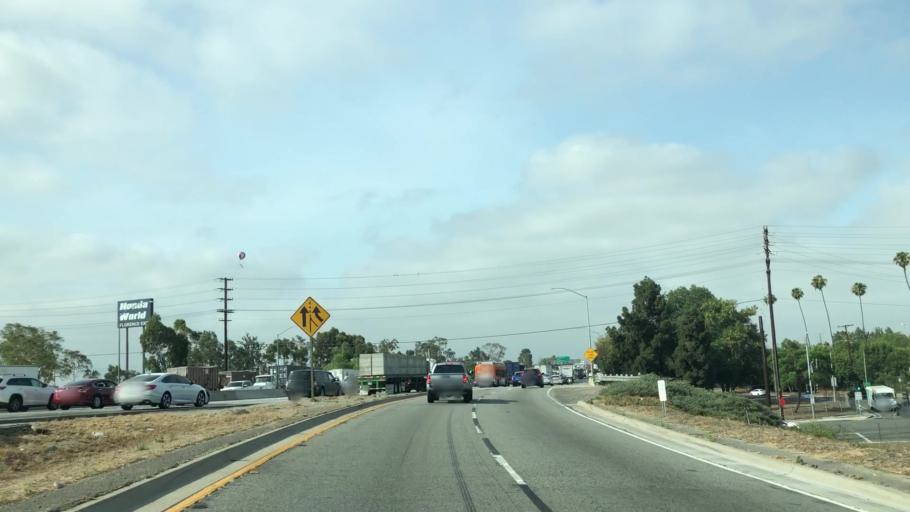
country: US
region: California
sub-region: Los Angeles County
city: Santa Fe Springs
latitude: 33.9389
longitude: -118.0982
